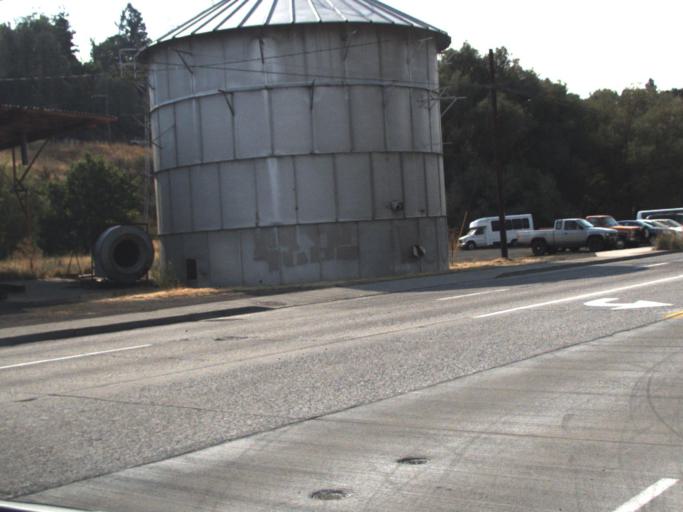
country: US
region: Washington
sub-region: Whitman County
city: Pullman
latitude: 46.7377
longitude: -117.1744
